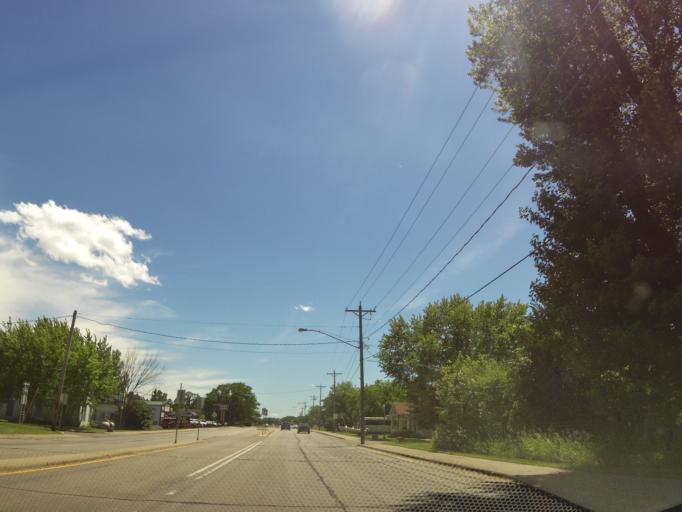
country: US
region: Minnesota
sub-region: Todd County
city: Staples
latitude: 46.3341
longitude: -94.6467
